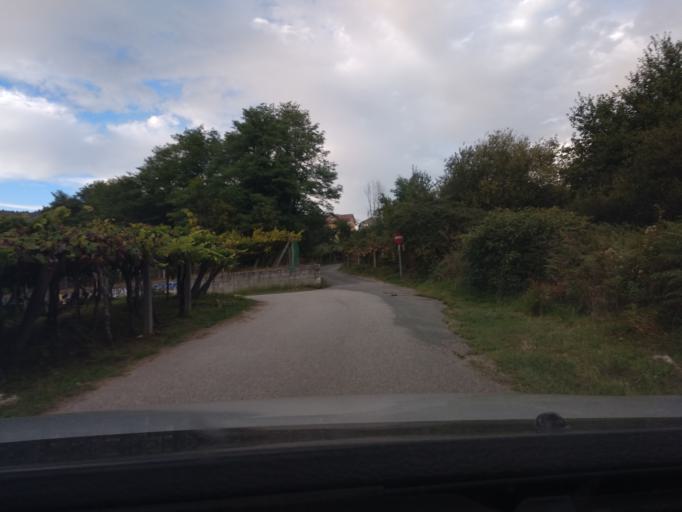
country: ES
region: Galicia
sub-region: Provincia de Pontevedra
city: Moana
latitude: 42.2969
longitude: -8.7344
